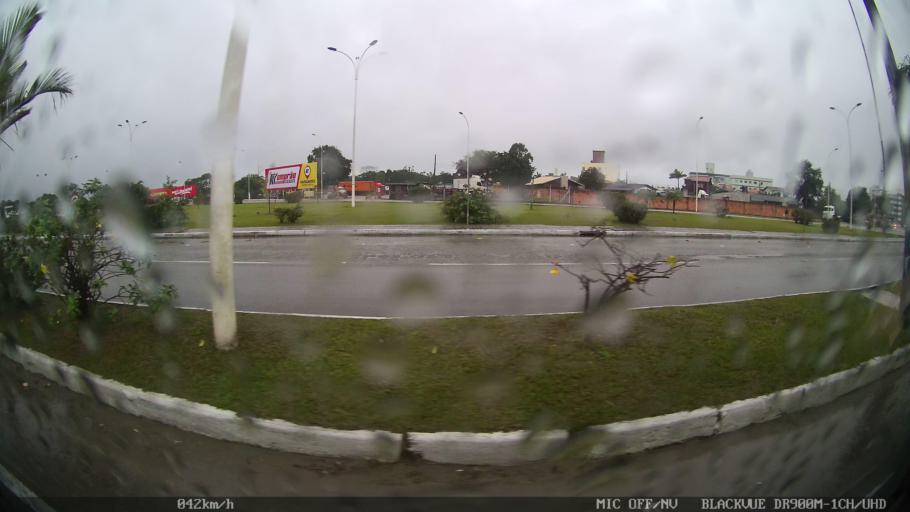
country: BR
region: Santa Catarina
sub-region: Navegantes
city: Navegantes
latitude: -26.8911
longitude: -48.6616
